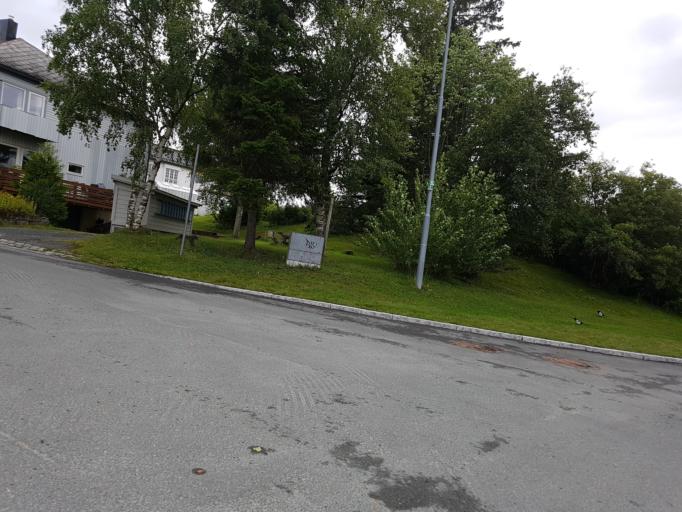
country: NO
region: Sor-Trondelag
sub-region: Trondheim
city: Trondheim
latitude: 63.4165
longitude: 10.4269
